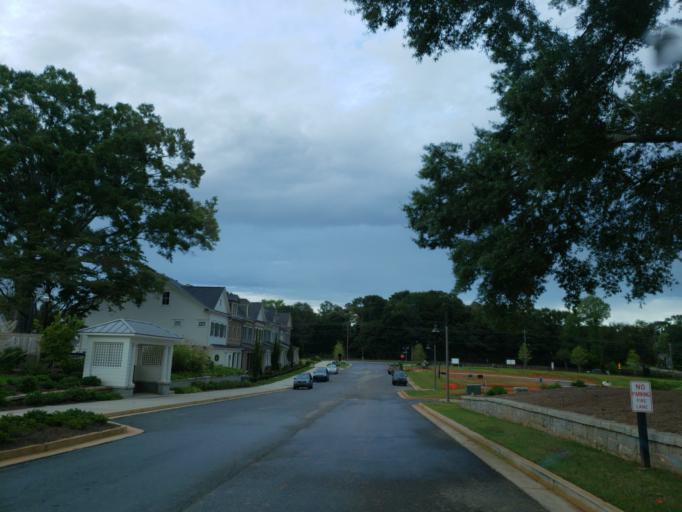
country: US
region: Georgia
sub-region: Cherokee County
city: Woodstock
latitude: 34.0922
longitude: -84.5217
